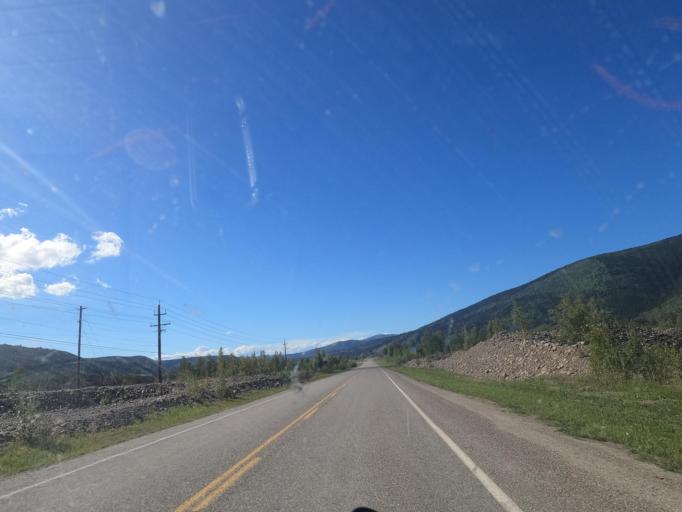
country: CA
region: Yukon
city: Dawson City
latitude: 64.0350
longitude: -139.2878
